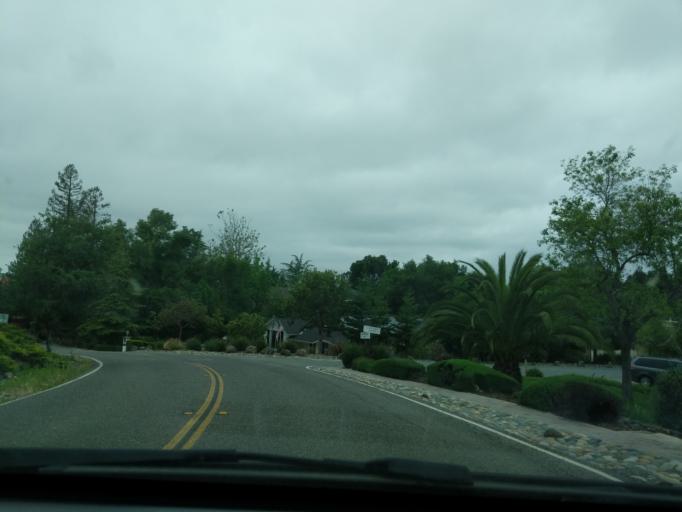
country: US
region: California
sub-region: Santa Clara County
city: San Martin
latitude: 37.1449
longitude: -121.5866
